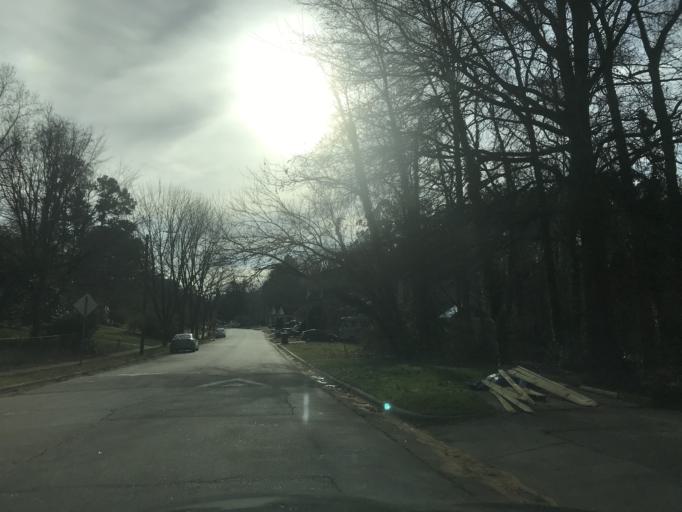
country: US
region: North Carolina
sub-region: Wake County
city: Raleigh
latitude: 35.8302
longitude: -78.5899
